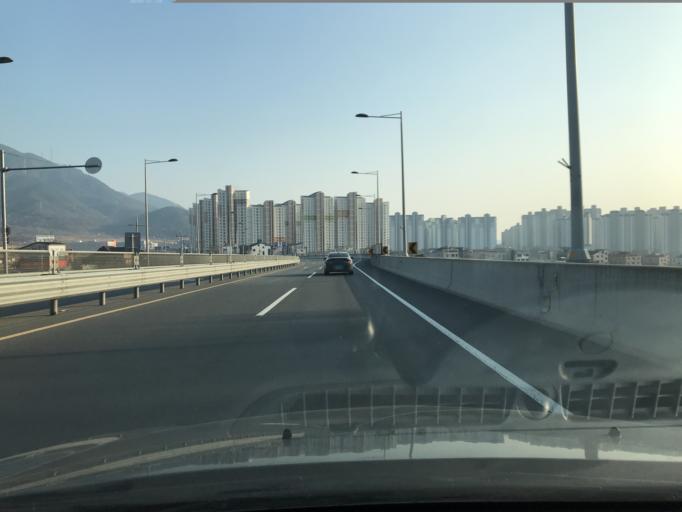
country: KR
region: Daegu
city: Hwawon
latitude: 35.7049
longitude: 128.4658
